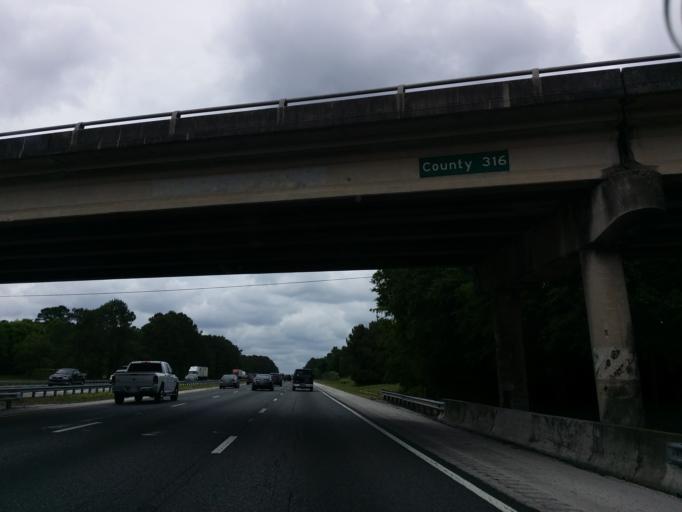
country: US
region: Florida
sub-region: Marion County
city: Citra
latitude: 29.3667
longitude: -82.2262
